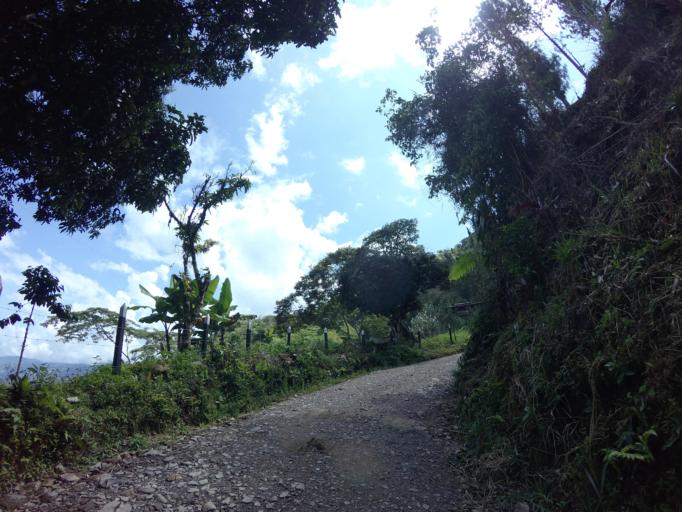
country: CO
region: Antioquia
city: Narino
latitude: 5.5162
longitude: -75.1719
